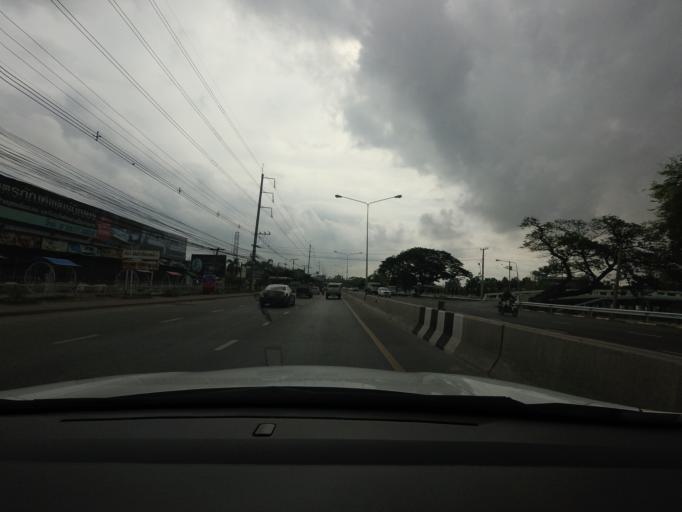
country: TH
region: Pathum Thani
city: Ban Rangsit
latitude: 14.0300
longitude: 100.7586
